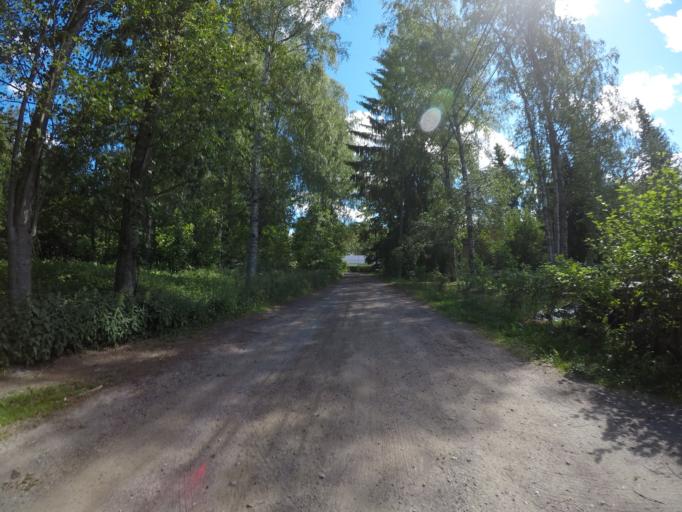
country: FI
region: Haeme
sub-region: Haemeenlinna
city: Haemeenlinna
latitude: 61.0196
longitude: 24.4369
